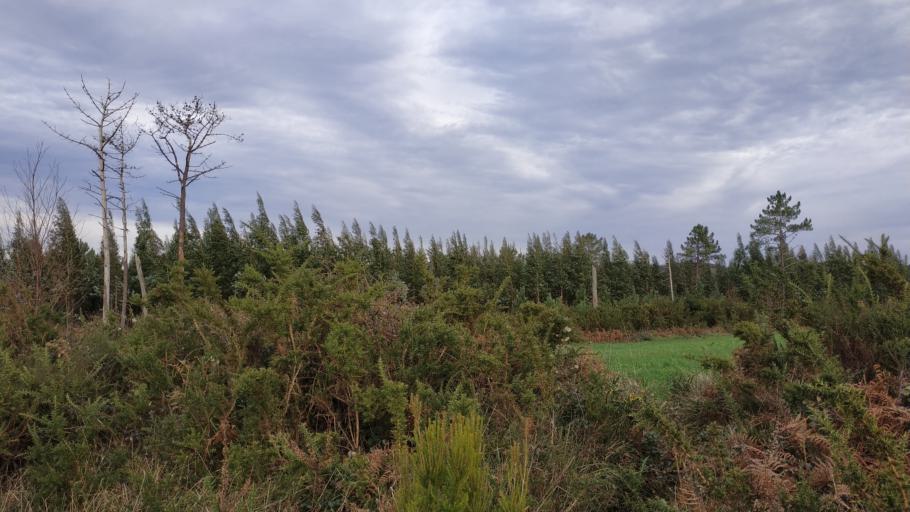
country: ES
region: Galicia
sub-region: Provincia de Pontevedra
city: Silleda
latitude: 42.7739
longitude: -8.1647
